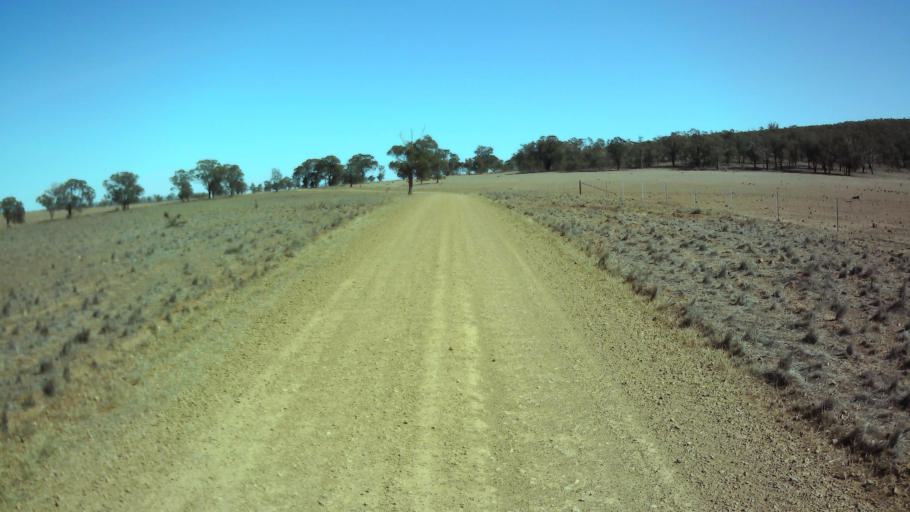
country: AU
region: New South Wales
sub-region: Weddin
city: Grenfell
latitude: -33.7615
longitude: 147.9225
